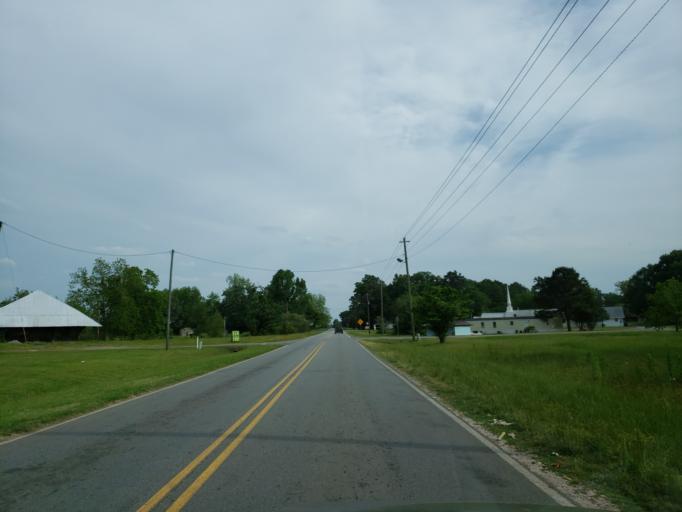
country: US
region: Georgia
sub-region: Dooly County
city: Vienna
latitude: 32.1472
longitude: -83.8779
